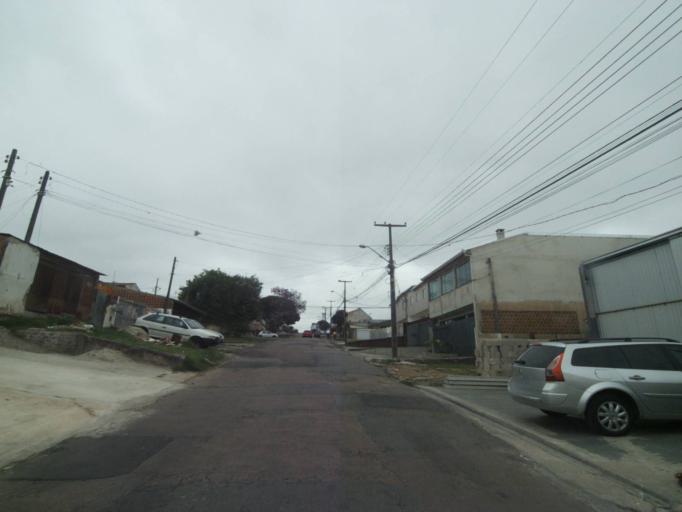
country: BR
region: Parana
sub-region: Sao Jose Dos Pinhais
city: Sao Jose dos Pinhais
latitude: -25.5420
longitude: -49.2895
